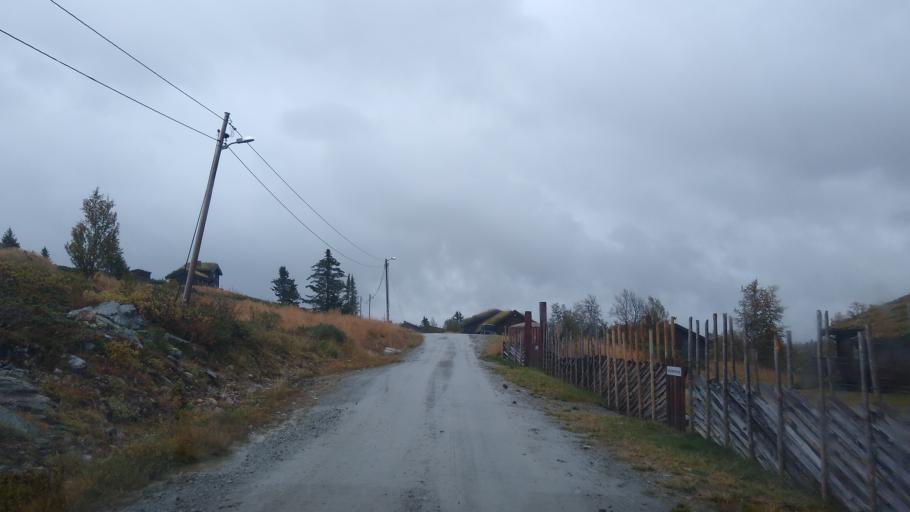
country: NO
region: Oppland
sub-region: Ringebu
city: Ringebu
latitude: 61.6725
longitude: 10.0955
